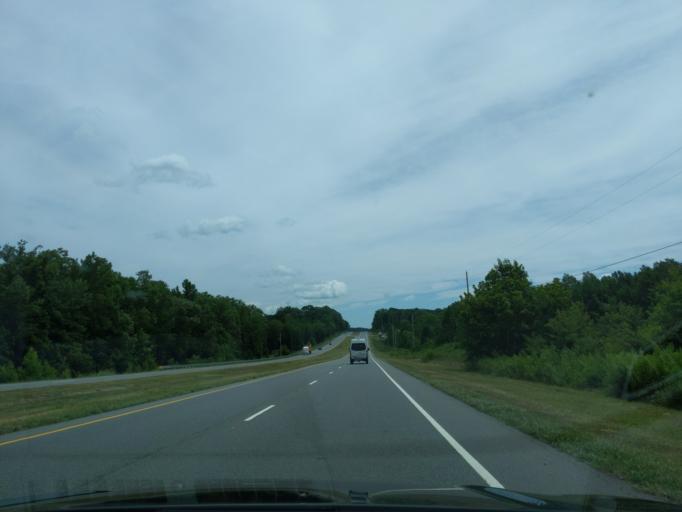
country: US
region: North Carolina
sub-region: Cabarrus County
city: Mount Pleasant
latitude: 35.3969
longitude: -80.4759
